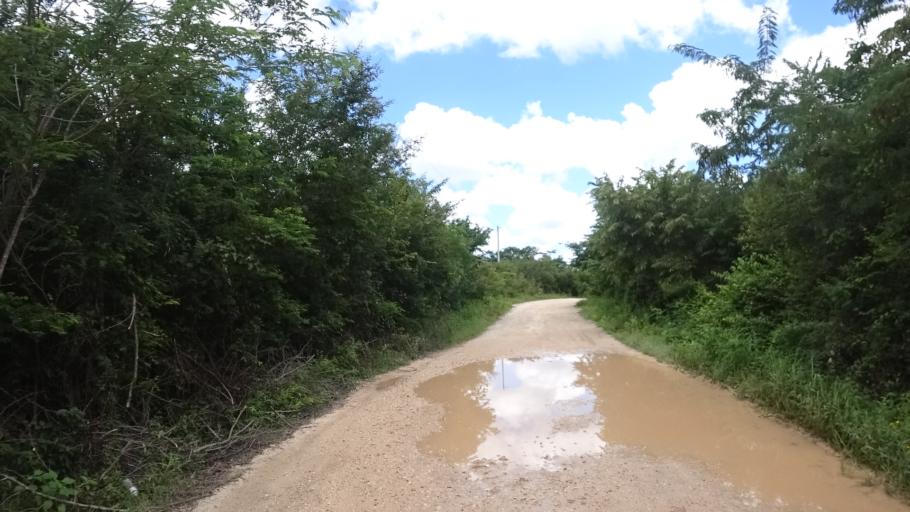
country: MX
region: Yucatan
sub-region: Valladolid
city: Dzitnup
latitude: 20.6720
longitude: -88.2283
